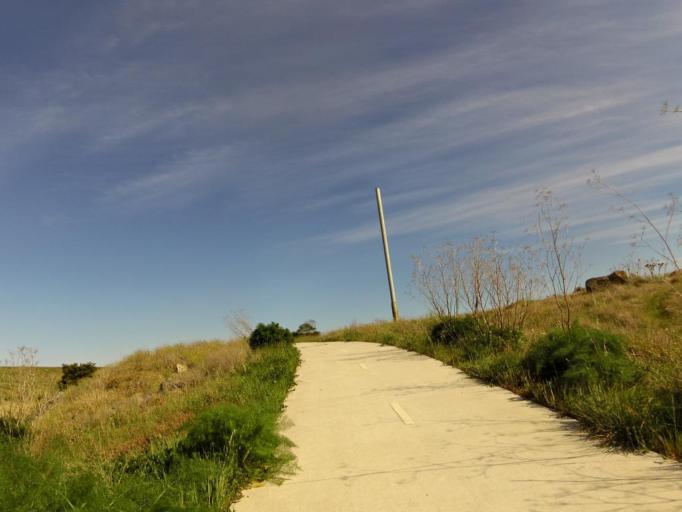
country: AU
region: Victoria
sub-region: Brimbank
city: Brooklyn
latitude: -37.8134
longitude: 144.8278
